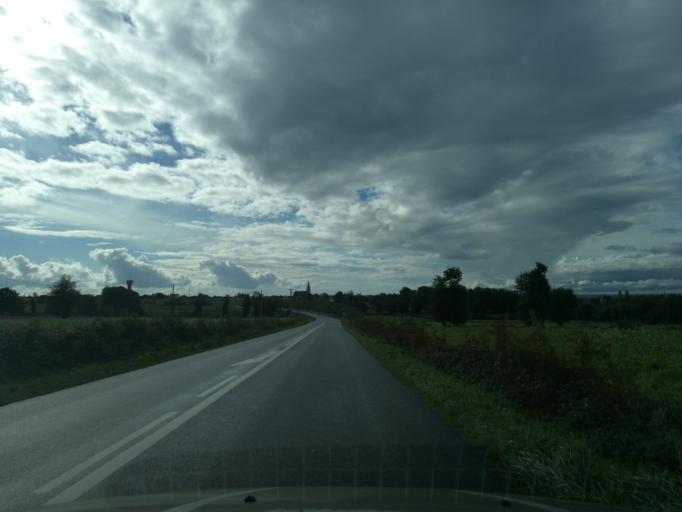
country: FR
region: Brittany
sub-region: Departement d'Ille-et-Vilaine
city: Bedee
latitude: 48.1937
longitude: -1.9413
